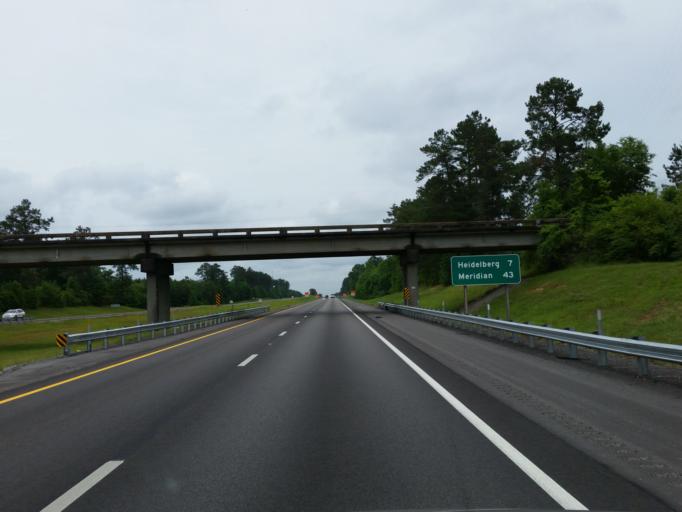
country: US
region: Mississippi
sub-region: Jones County
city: Sharon
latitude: 31.8127
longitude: -89.0525
